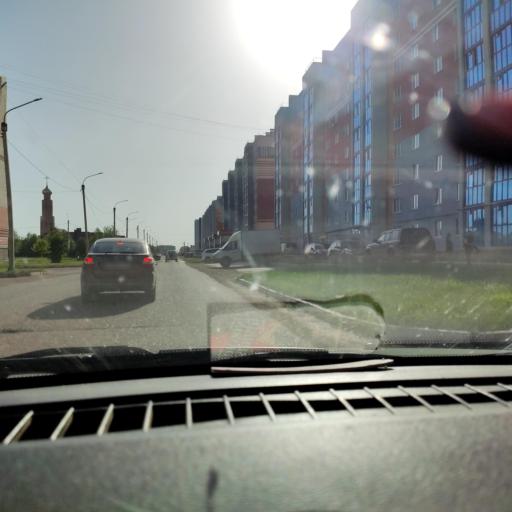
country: RU
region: Bashkortostan
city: Sterlitamak
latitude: 53.6376
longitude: 55.8999
